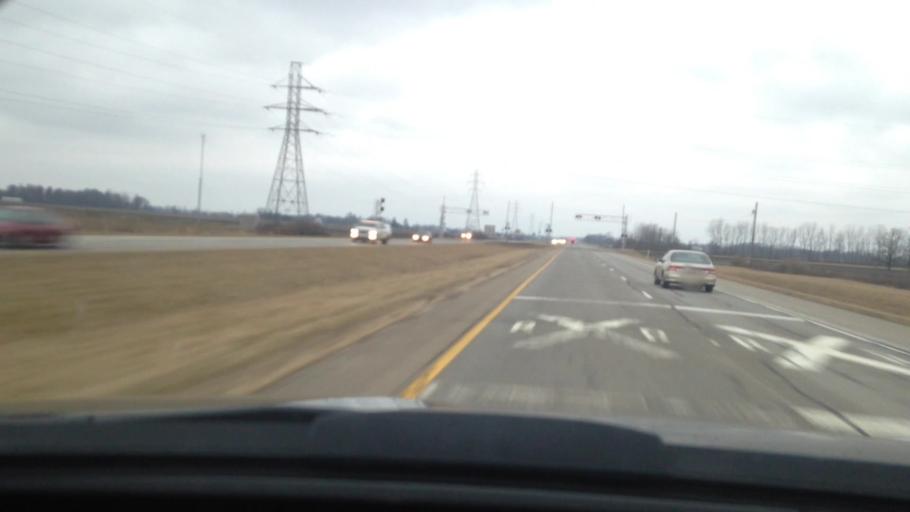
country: US
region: Indiana
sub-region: Delaware County
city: Muncie
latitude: 40.1423
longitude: -85.3881
